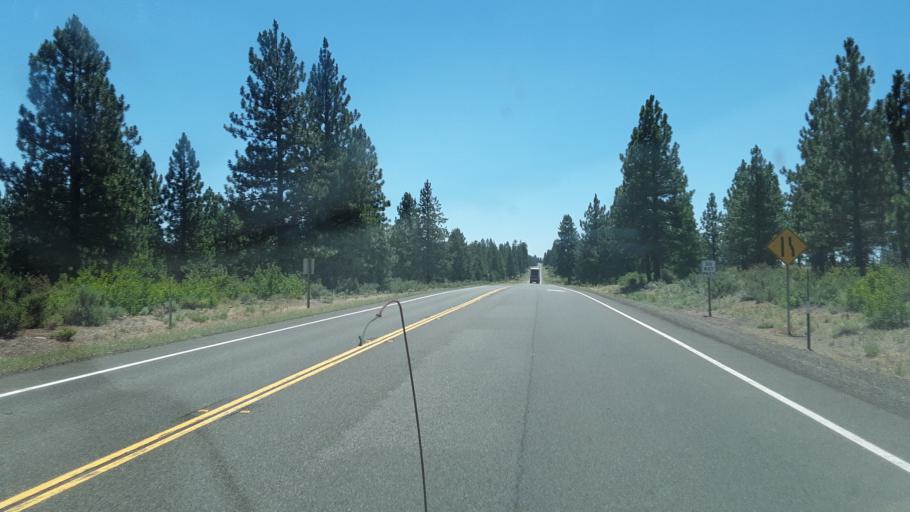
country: US
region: California
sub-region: Siskiyou County
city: Tulelake
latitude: 41.6020
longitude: -121.2056
